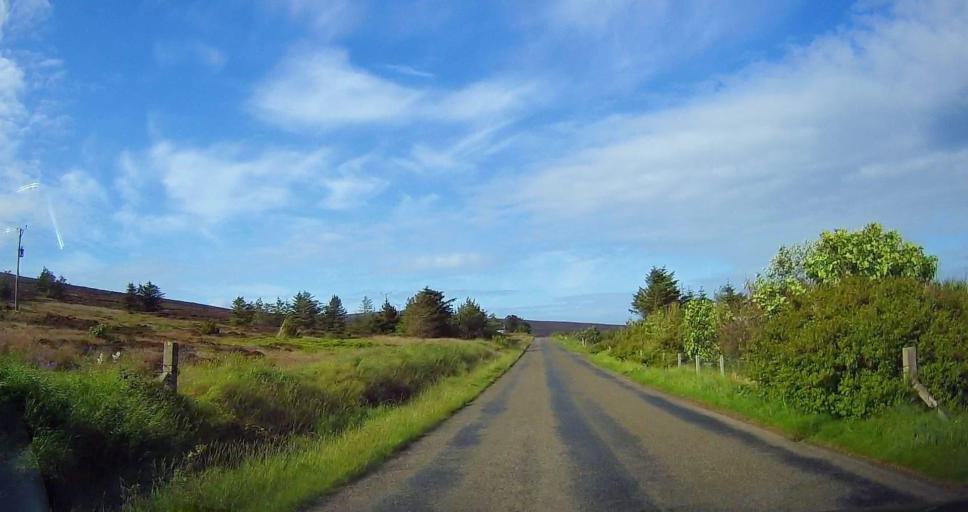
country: GB
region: Scotland
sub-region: Orkney Islands
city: Stromness
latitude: 58.7941
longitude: -3.2547
